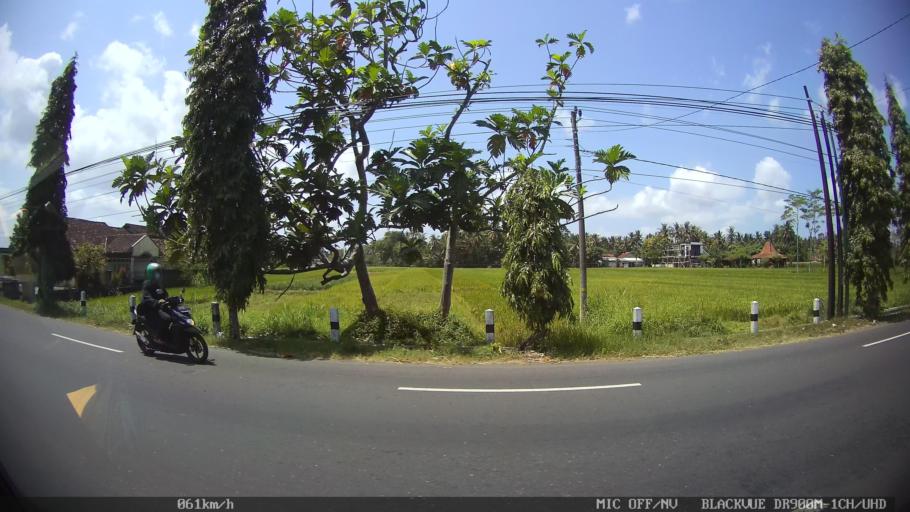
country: ID
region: Daerah Istimewa Yogyakarta
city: Pandak
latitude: -7.9157
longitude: 110.2856
